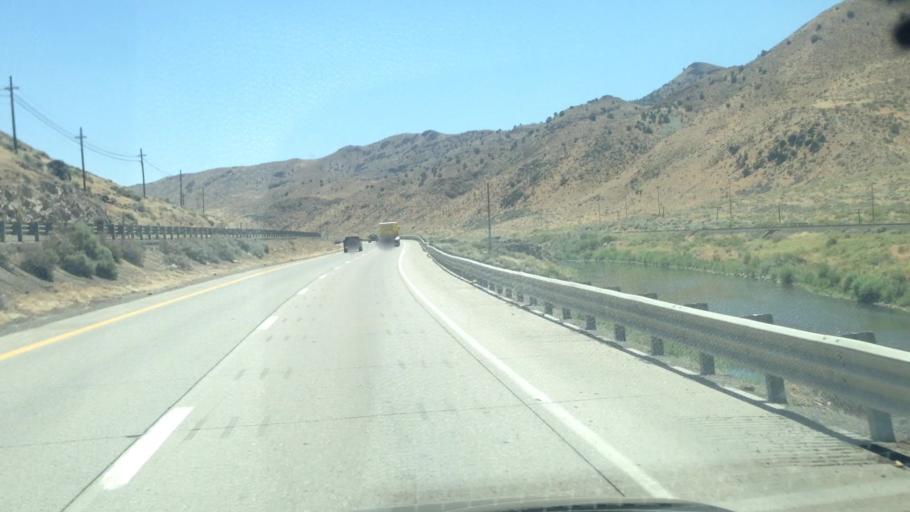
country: US
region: Nevada
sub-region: Washoe County
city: Sparks
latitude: 39.5189
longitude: -119.6846
